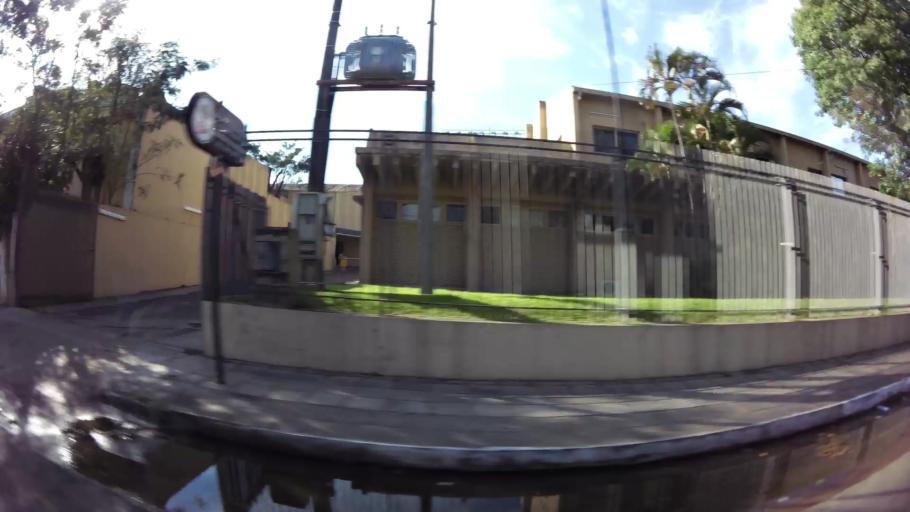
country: PY
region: Asuncion
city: Asuncion
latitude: -25.2766
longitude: -57.6113
